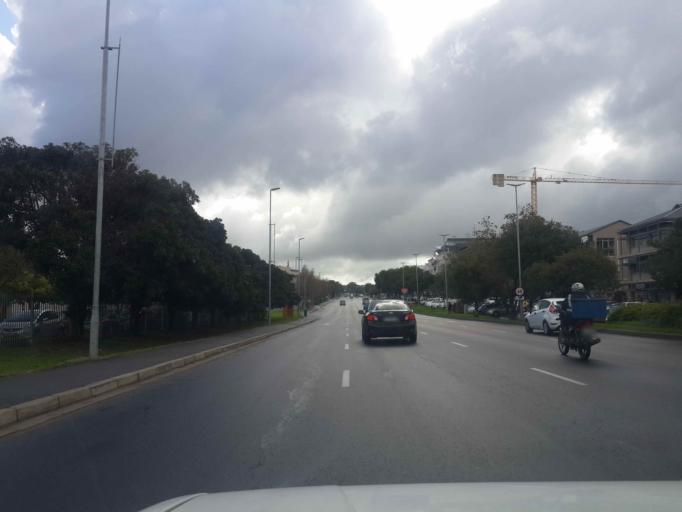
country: ZA
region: Western Cape
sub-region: City of Cape Town
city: Kraaifontein
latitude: -33.8839
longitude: 18.6347
